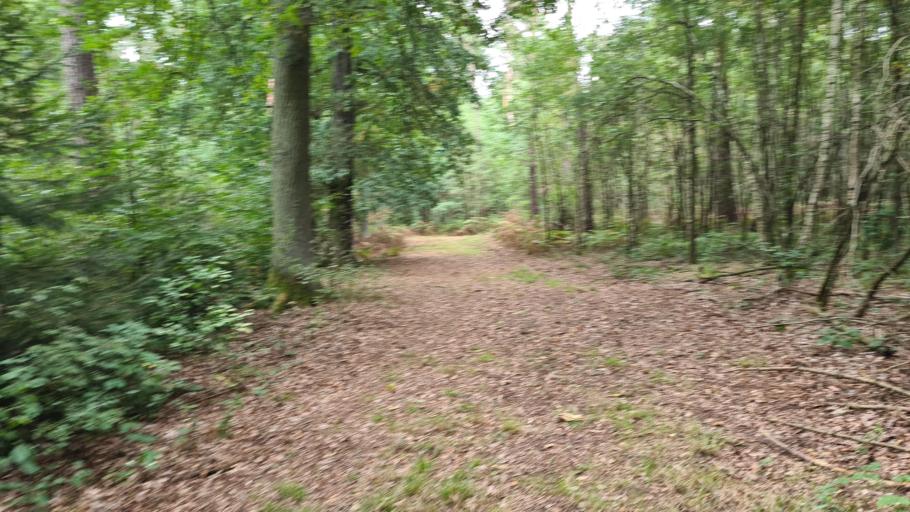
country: DE
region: Brandenburg
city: Doberlug-Kirchhain
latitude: 51.6241
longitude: 13.5265
